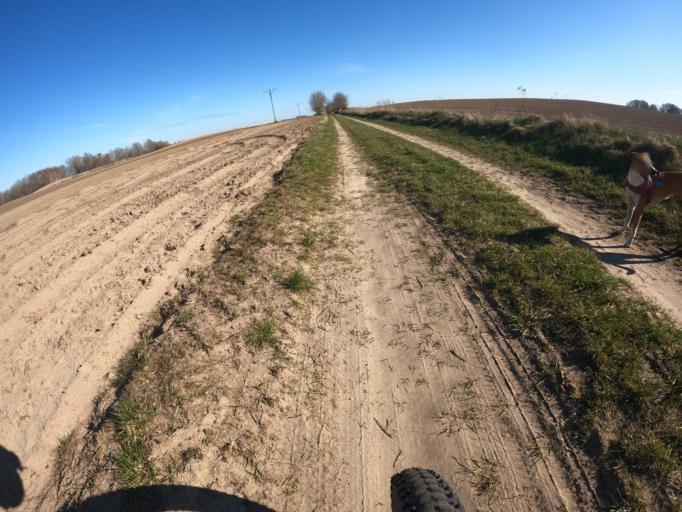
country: PL
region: West Pomeranian Voivodeship
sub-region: Powiat kolobrzeski
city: Ryman
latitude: 54.0220
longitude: 15.4715
